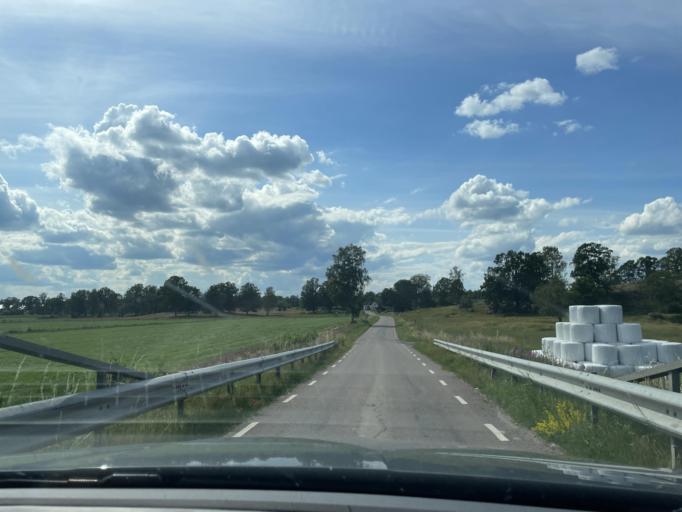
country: SE
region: Kalmar
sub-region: Vimmerby Kommun
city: Sodra Vi
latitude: 57.8157
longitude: 15.7643
